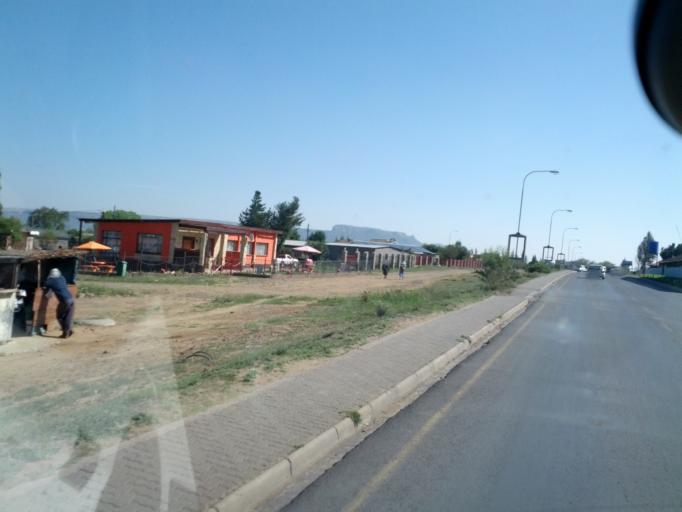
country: LS
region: Maseru
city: Maseru
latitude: -29.3050
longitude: 27.4998
